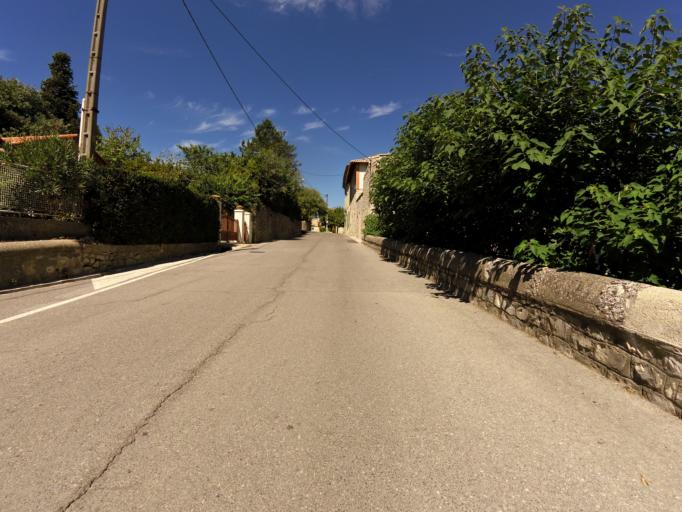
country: FR
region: Languedoc-Roussillon
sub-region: Departement du Gard
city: Quissac
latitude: 43.8725
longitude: 4.0414
